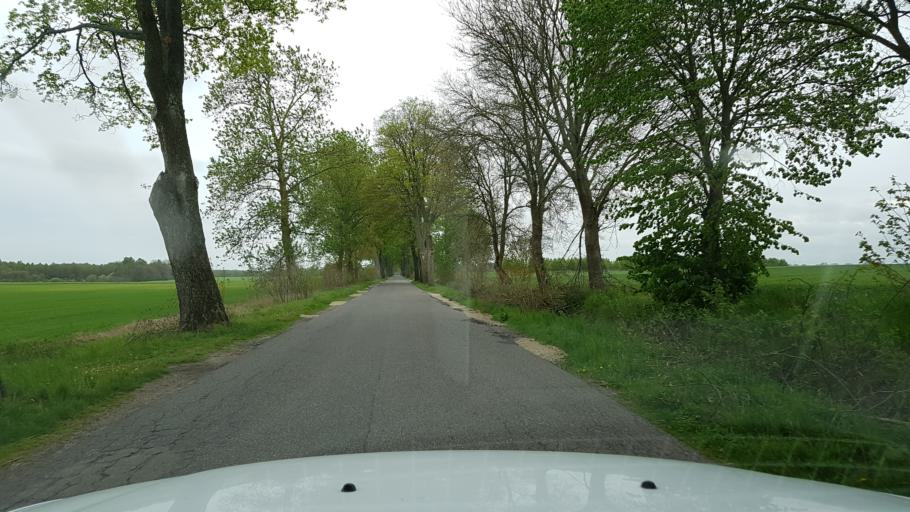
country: PL
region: West Pomeranian Voivodeship
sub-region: Powiat slawienski
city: Slawno
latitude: 54.4231
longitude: 16.7331
